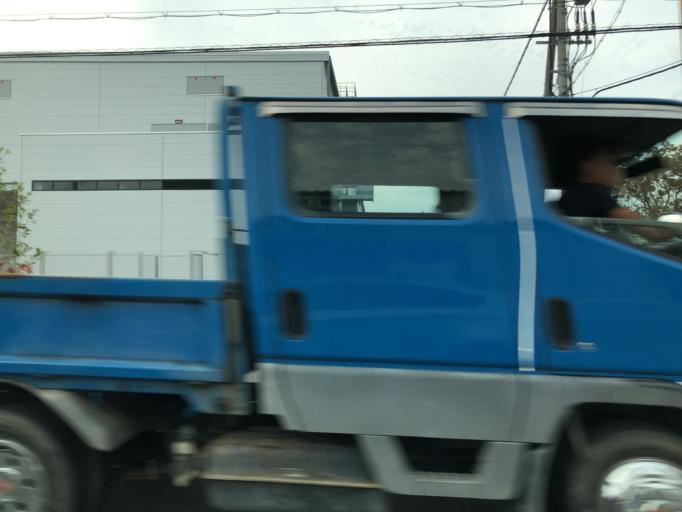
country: JP
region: Hyogo
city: Ashiya
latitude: 34.6881
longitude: 135.2586
